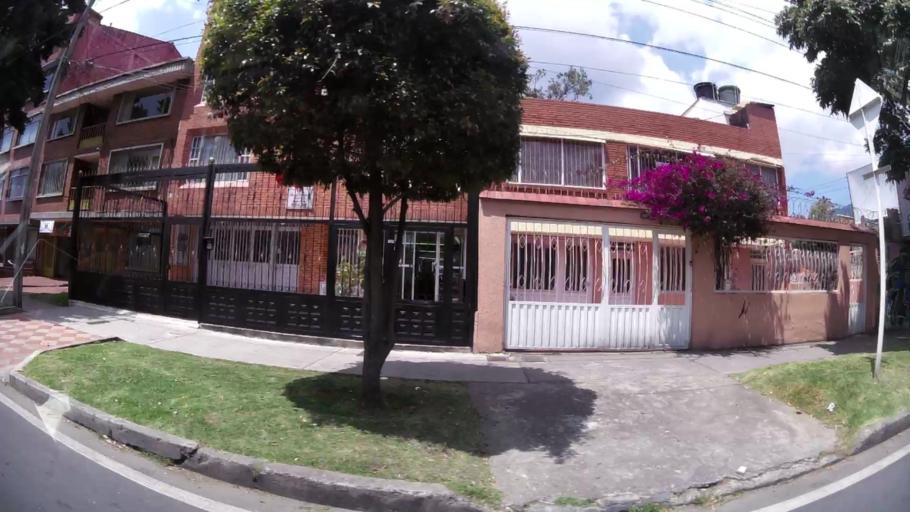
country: CO
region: Bogota D.C.
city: Bogota
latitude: 4.5830
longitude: -74.0913
